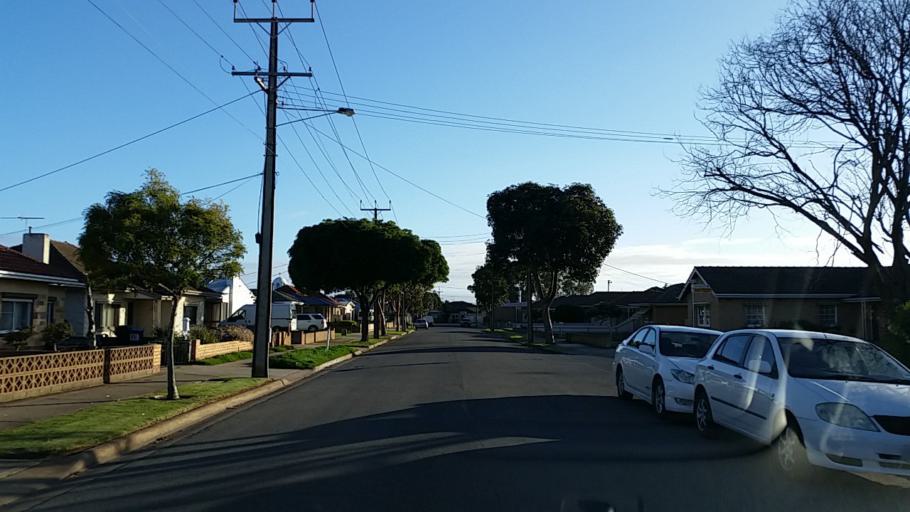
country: AU
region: South Australia
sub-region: Charles Sturt
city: Findon
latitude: -34.8961
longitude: 138.5368
